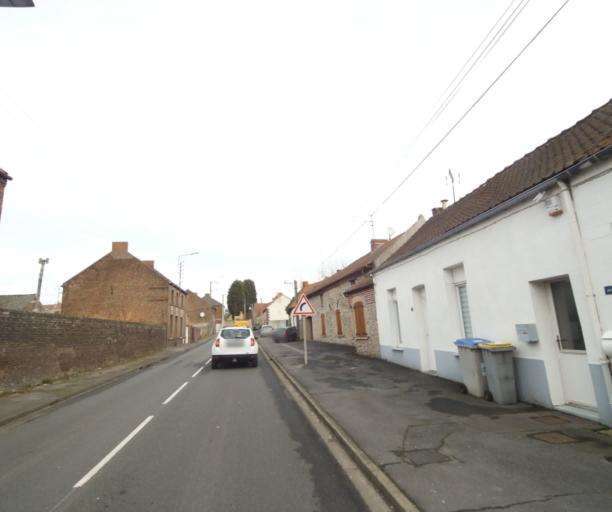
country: BE
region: Wallonia
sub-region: Province du Hainaut
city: Peruwelz
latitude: 50.4875
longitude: 3.5829
